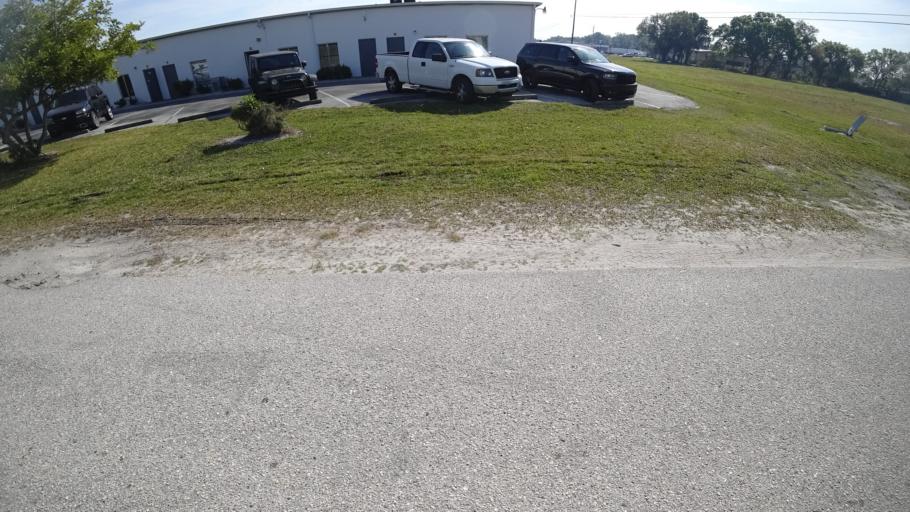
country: US
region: Florida
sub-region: Manatee County
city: Whitfield
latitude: 27.4075
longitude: -82.5488
